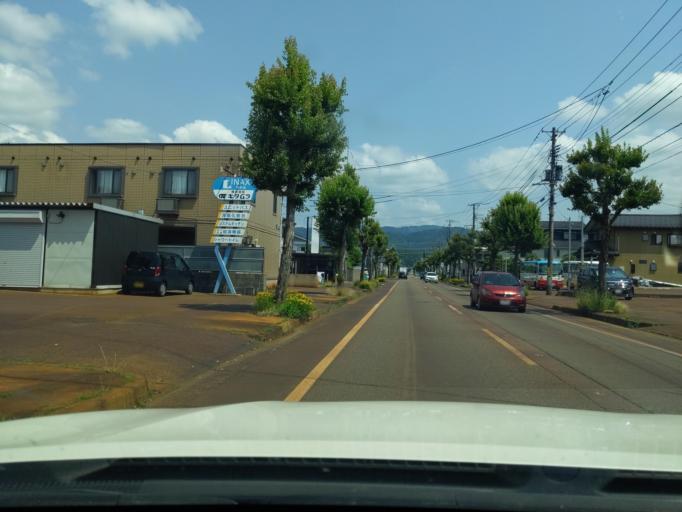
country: JP
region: Niigata
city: Nagaoka
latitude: 37.4303
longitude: 138.8541
